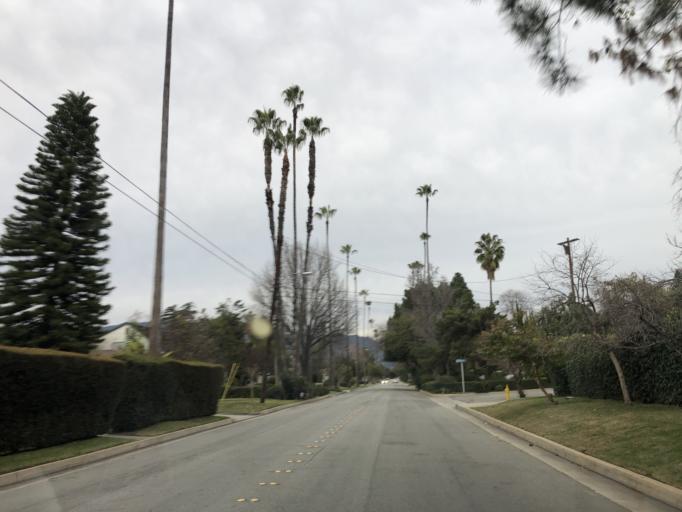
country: US
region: California
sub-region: Los Angeles County
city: San Marino
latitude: 34.1168
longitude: -118.0967
